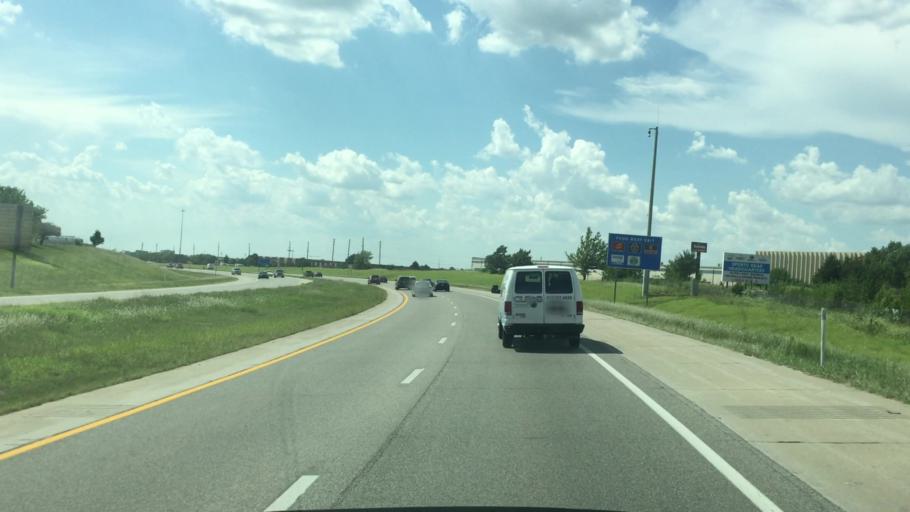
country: US
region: Kansas
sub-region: Sedgwick County
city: Bellaire
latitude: 37.7438
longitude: -97.2340
